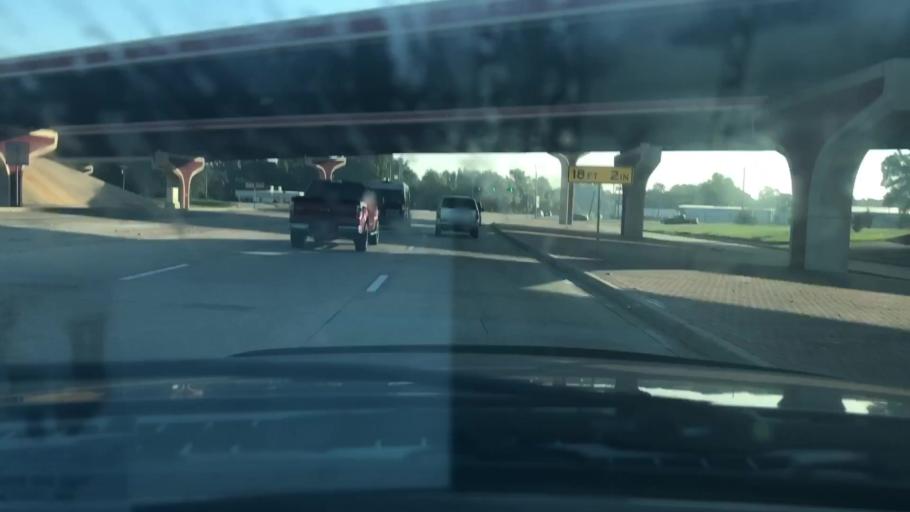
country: US
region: Texas
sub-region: Bowie County
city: Wake Village
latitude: 33.3943
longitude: -94.0983
